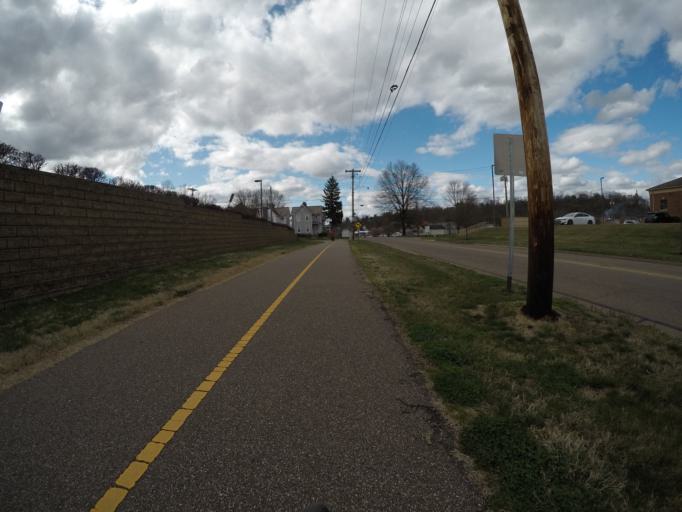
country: US
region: West Virginia
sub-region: Wood County
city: Williamstown
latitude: 39.4118
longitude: -81.4386
